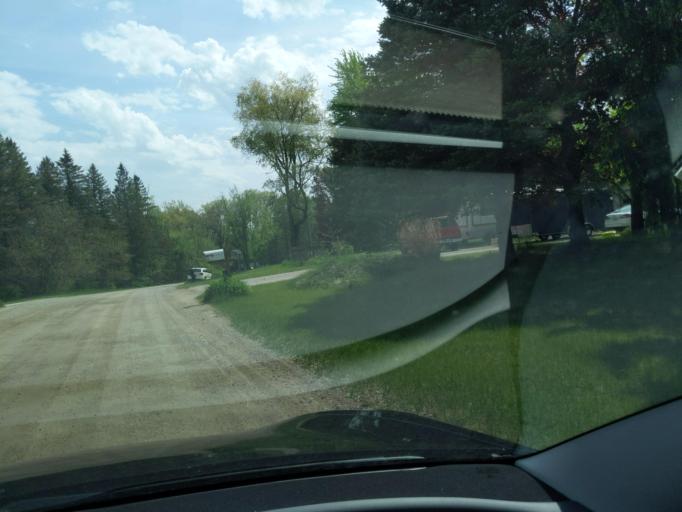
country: US
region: Michigan
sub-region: Ingham County
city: Stockbridge
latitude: 42.4299
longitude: -84.0733
